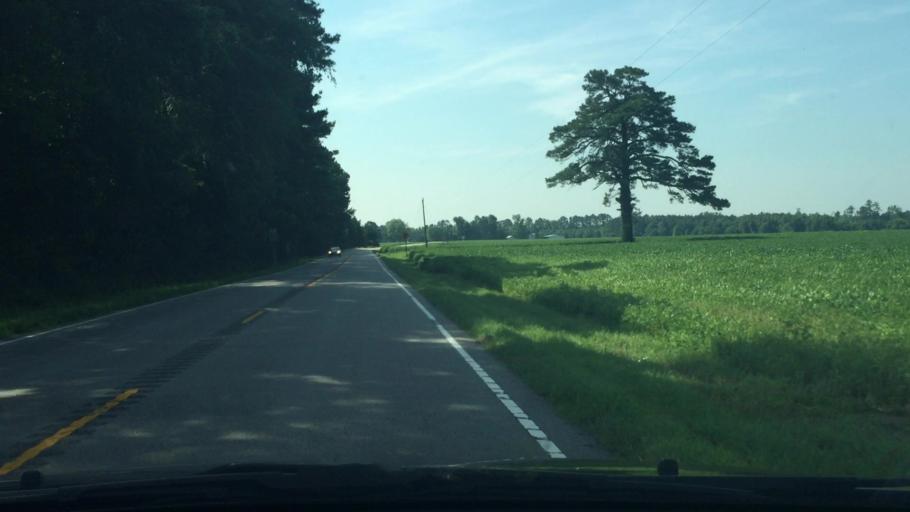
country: US
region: Virginia
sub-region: Southampton County
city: Courtland
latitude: 36.8492
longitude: -77.1334
